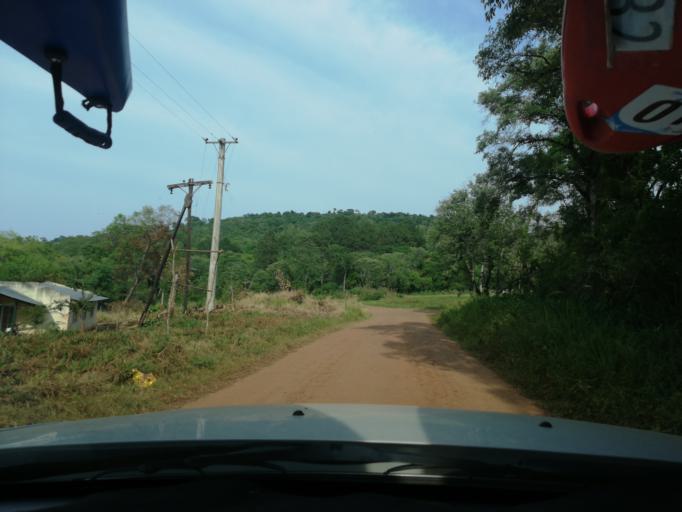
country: AR
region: Misiones
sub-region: Departamento de San Ignacio
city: San Ignacio
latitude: -27.2938
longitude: -55.5671
